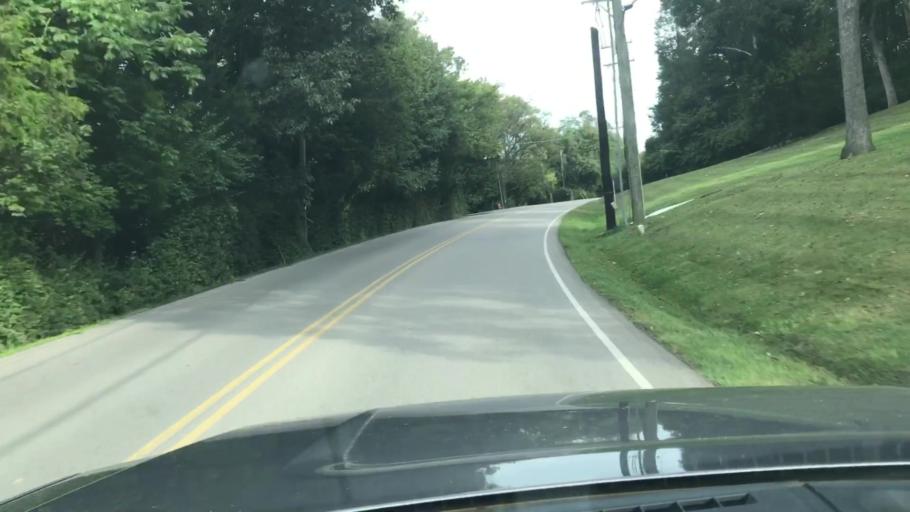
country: US
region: Tennessee
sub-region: Davidson County
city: Forest Hills
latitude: 36.0729
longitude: -86.8320
